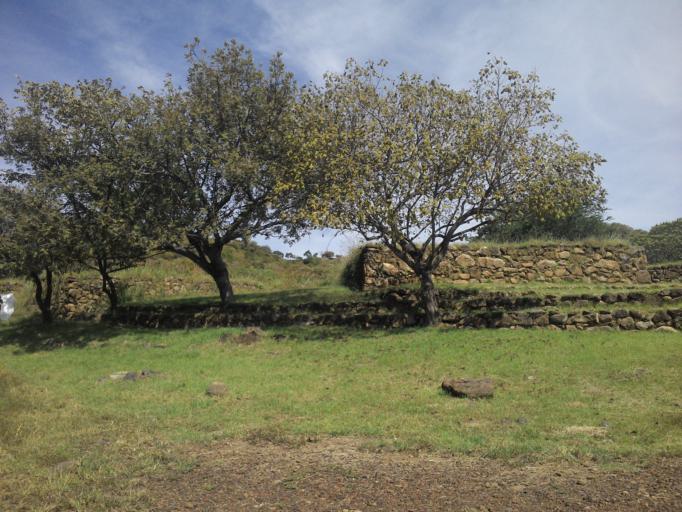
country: MX
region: Jalisco
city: Teuchitlan
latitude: 20.6958
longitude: -103.8371
